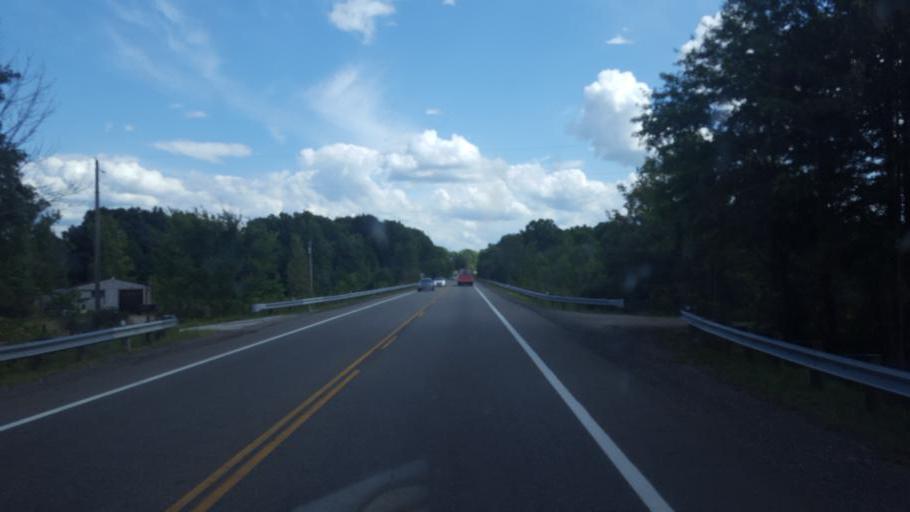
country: US
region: Ohio
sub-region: Portage County
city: Ravenna
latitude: 41.1730
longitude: -81.2278
